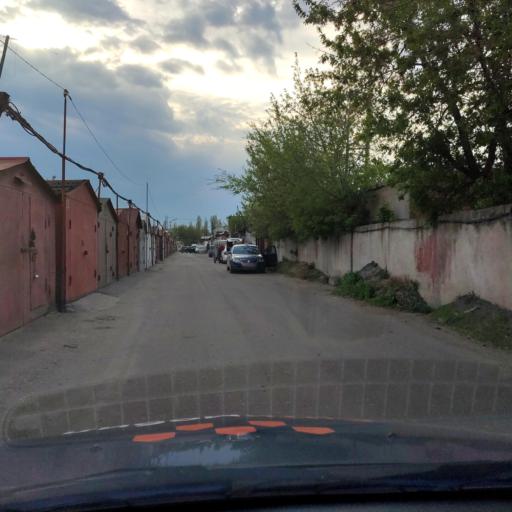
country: RU
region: Voronezj
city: Voronezh
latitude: 51.6459
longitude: 39.2723
